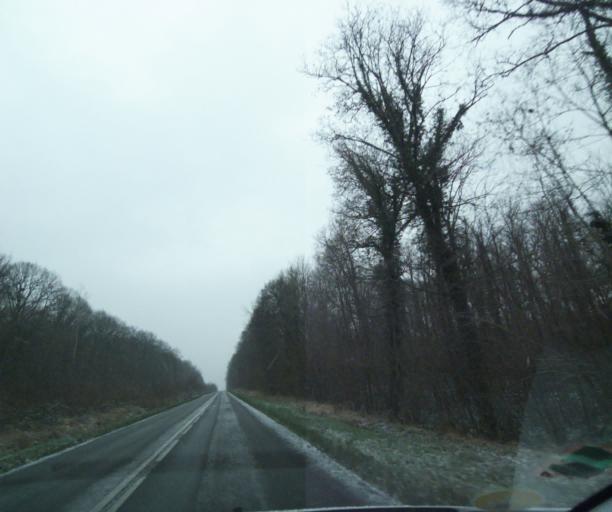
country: FR
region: Champagne-Ardenne
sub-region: Departement de la Haute-Marne
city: Wassy
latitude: 48.4761
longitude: 5.0147
